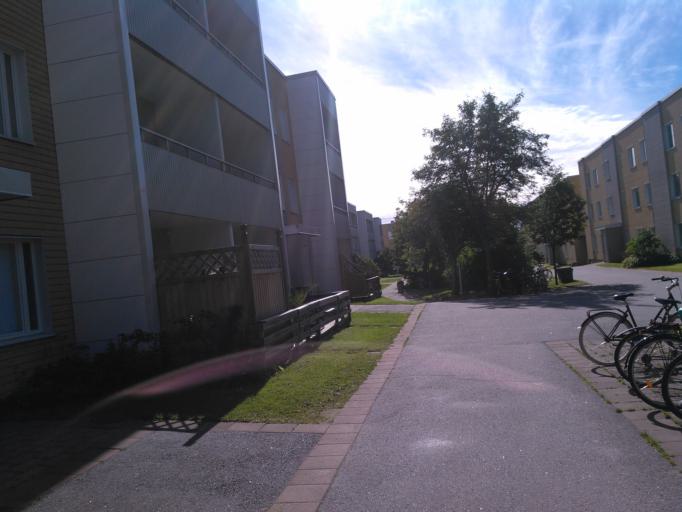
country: SE
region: Vaesterbotten
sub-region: Umea Kommun
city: Umea
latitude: 63.8010
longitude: 20.3243
